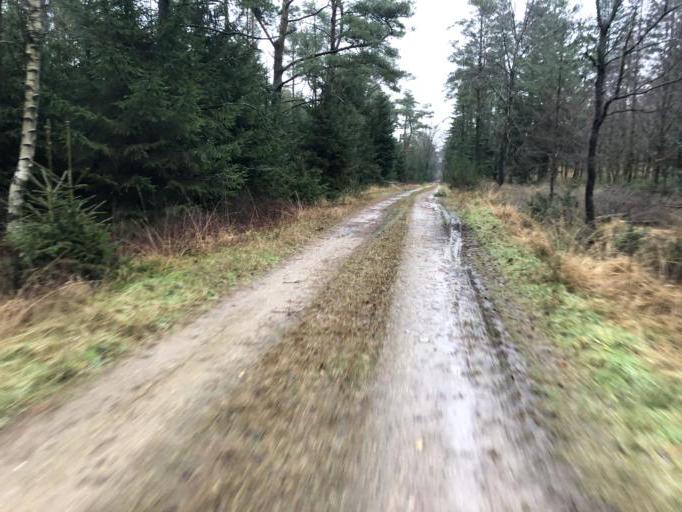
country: DK
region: Central Jutland
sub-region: Holstebro Kommune
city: Ulfborg
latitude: 56.2907
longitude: 8.4335
